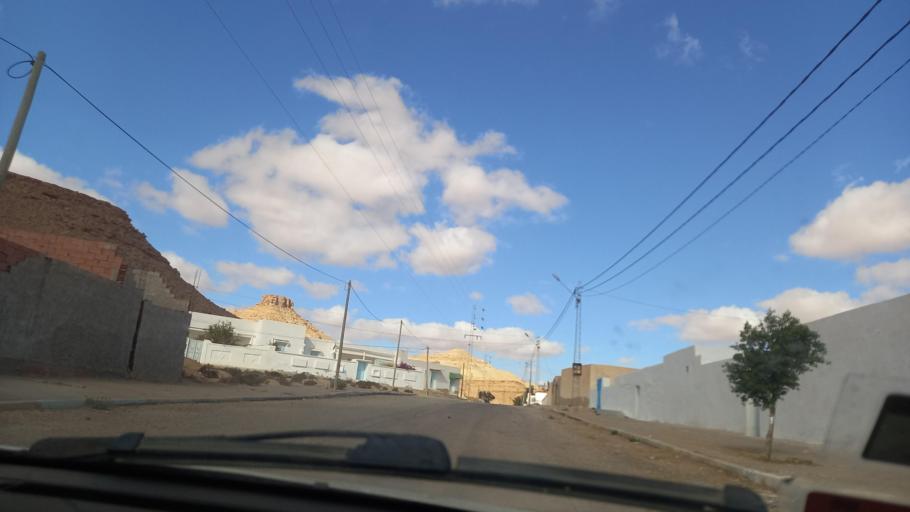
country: TN
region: Tataouine
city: Tataouine
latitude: 32.9823
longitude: 10.2640
